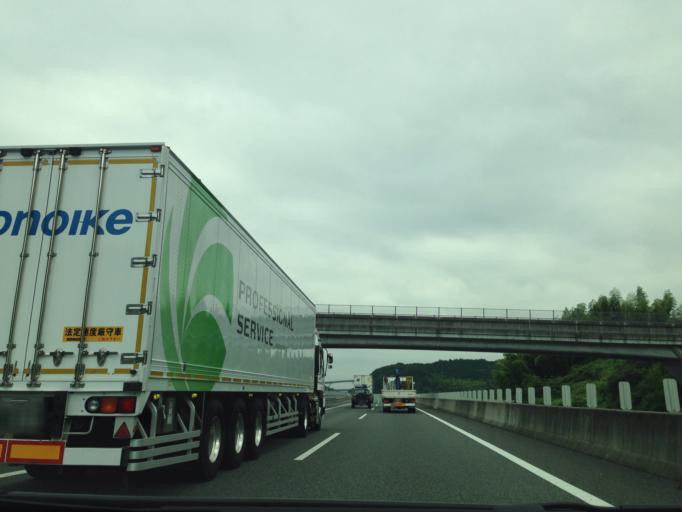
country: JP
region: Shizuoka
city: Fuji
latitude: 35.1711
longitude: 138.7471
